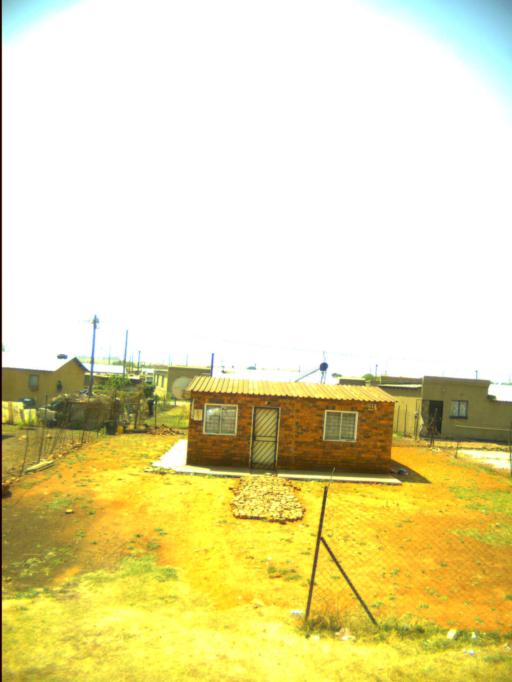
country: ZA
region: Mpumalanga
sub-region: Nkangala District Municipality
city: Delmas
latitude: -26.1409
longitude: 28.6909
